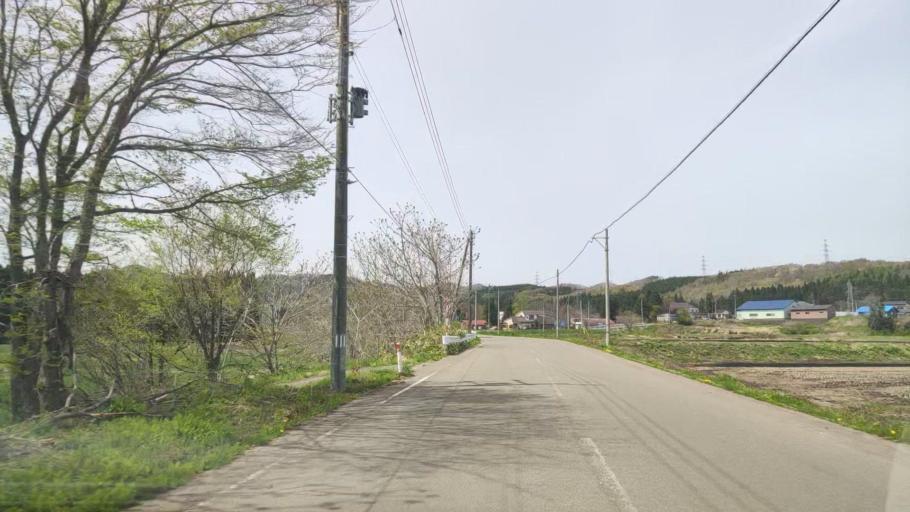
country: JP
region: Aomori
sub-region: Misawa Shi
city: Inuotose
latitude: 40.7863
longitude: 141.1114
